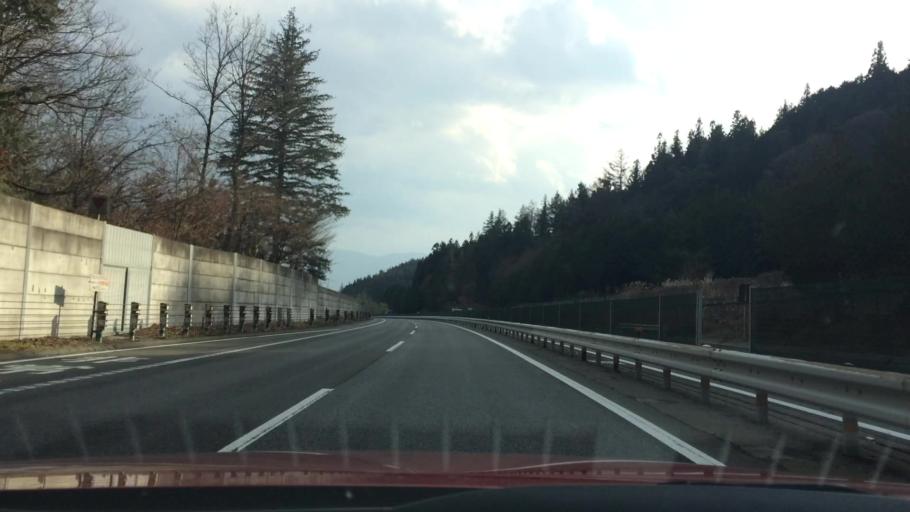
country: JP
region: Nagano
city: Ina
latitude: 35.7975
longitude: 137.9299
